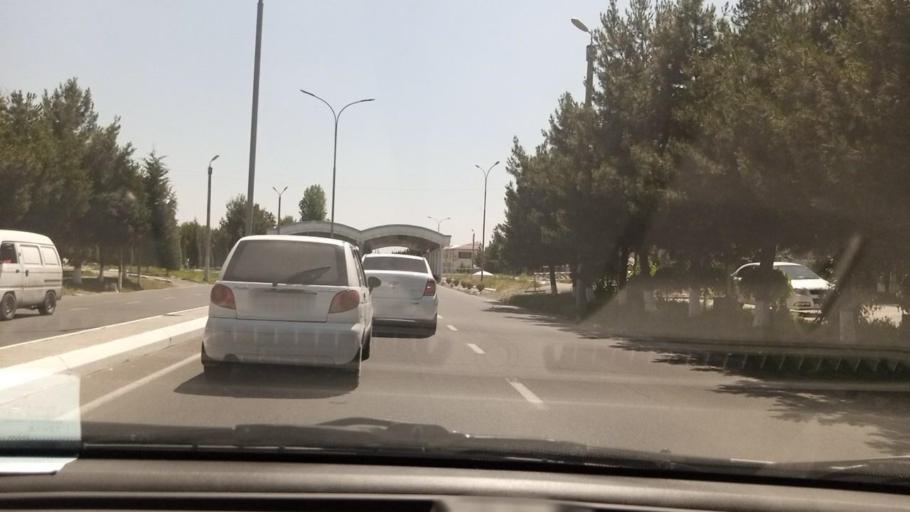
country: UZ
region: Toshkent
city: Urtaowul
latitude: 41.2159
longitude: 69.1734
